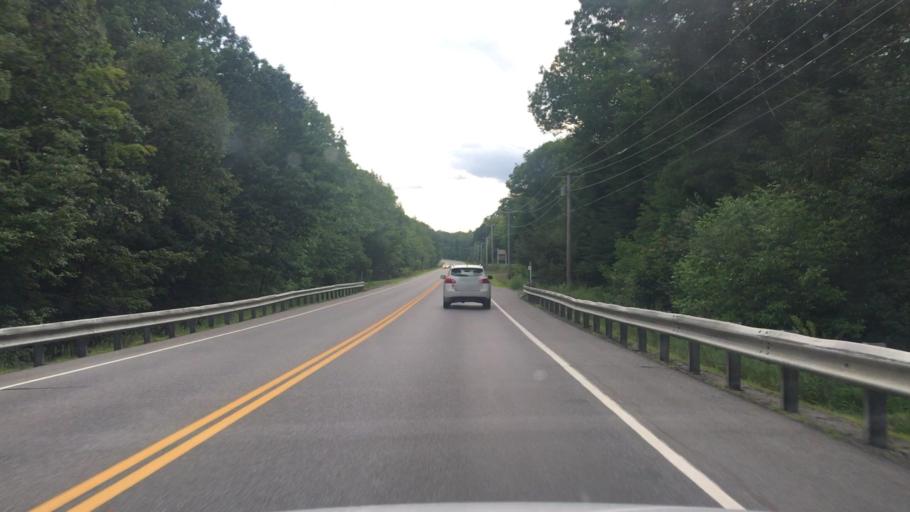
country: US
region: Maine
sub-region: Waldo County
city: Palermo
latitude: 44.4097
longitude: -69.5311
